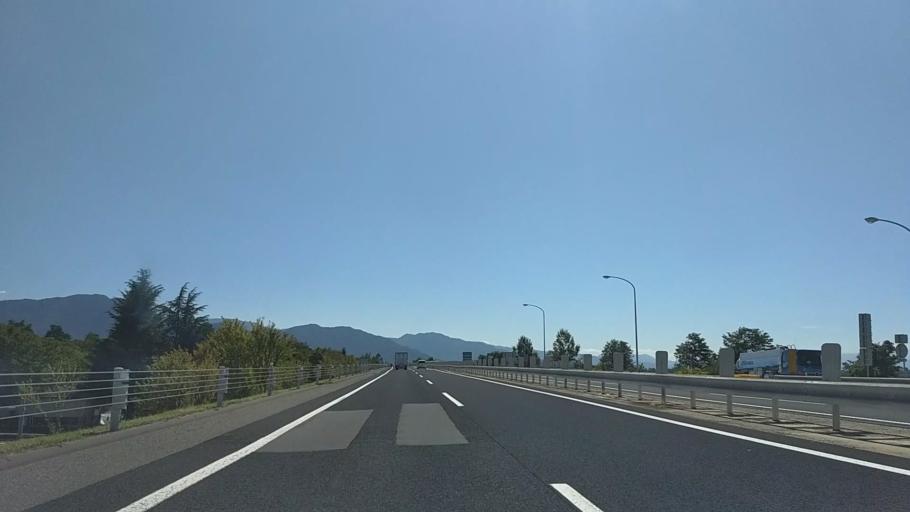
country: JP
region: Nagano
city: Suzaka
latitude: 36.6900
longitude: 138.2934
